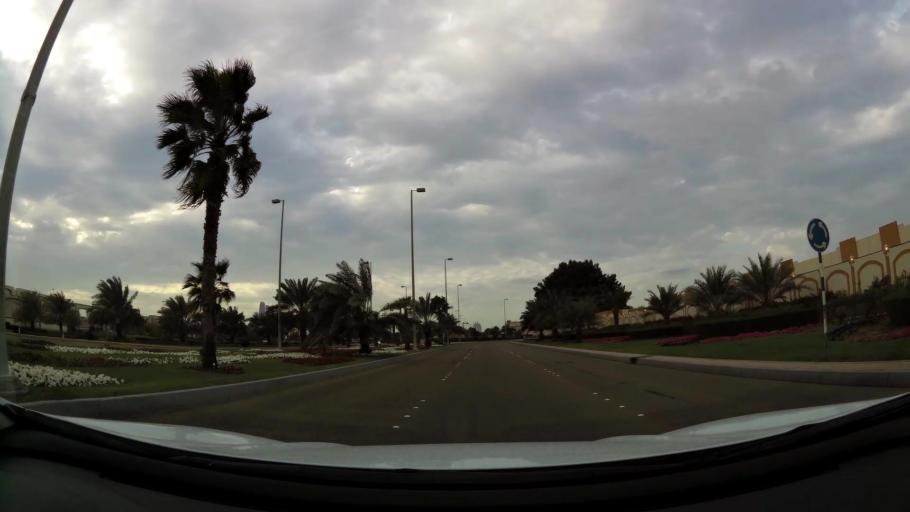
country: AE
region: Abu Dhabi
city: Abu Dhabi
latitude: 24.4466
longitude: 54.3556
